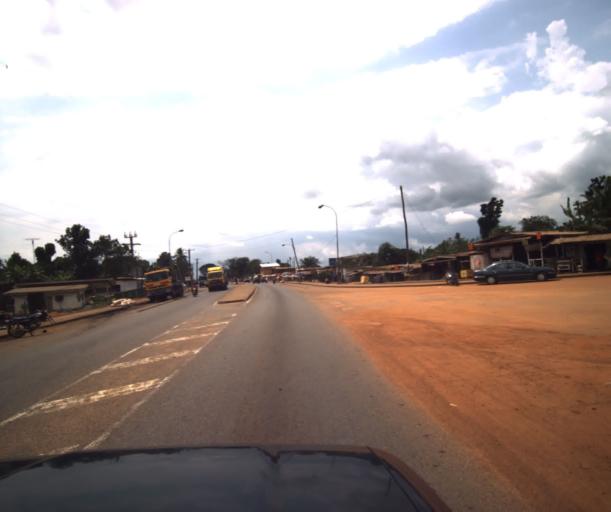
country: CM
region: Littoral
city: Edea
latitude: 3.7908
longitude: 10.1392
